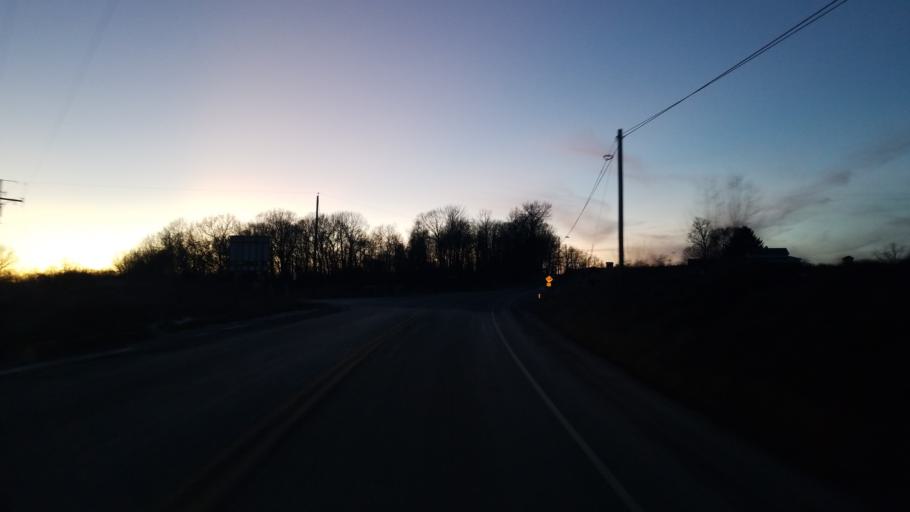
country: US
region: Pennsylvania
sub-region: Jefferson County
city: Punxsutawney
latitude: 40.8687
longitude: -79.1856
